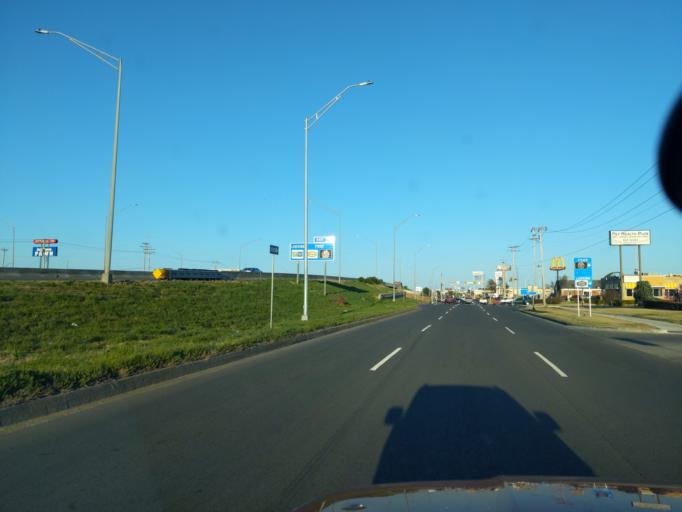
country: US
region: Oklahoma
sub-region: Cleveland County
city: Moore
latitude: 35.3911
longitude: -97.5319
